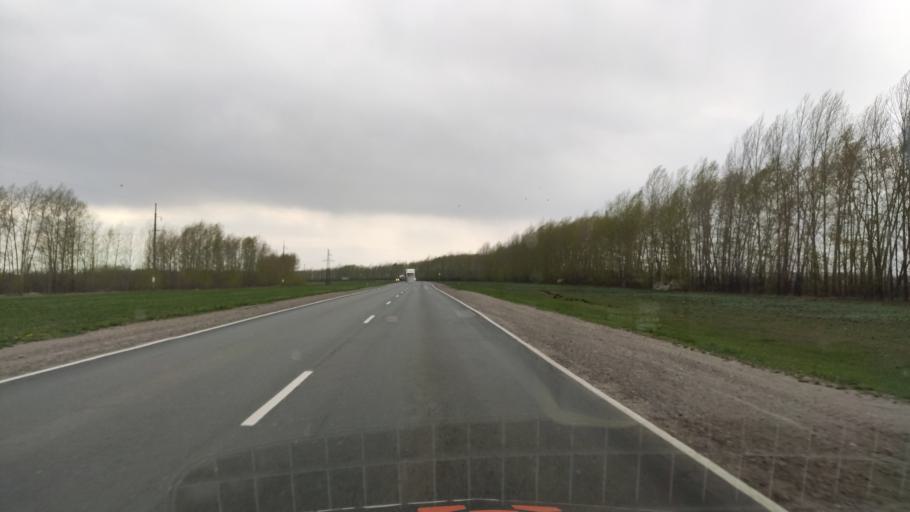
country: RU
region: Voronezj
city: Nizhnedevitsk
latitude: 51.5663
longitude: 38.4510
